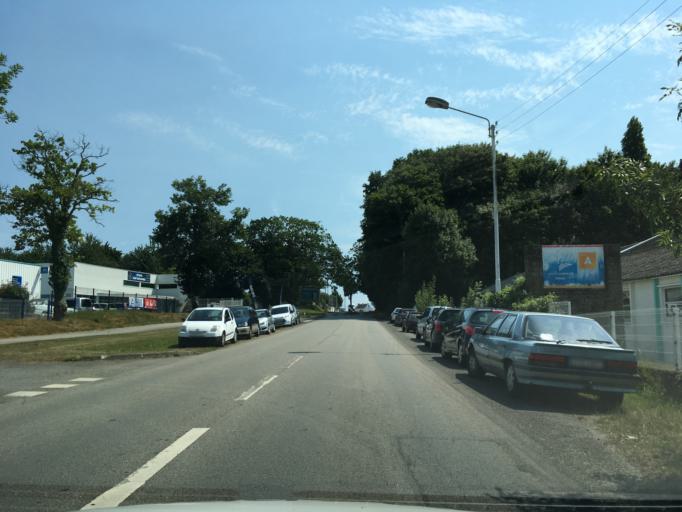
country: FR
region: Brittany
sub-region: Departement du Morbihan
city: Queven
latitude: 47.7703
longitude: -3.4039
